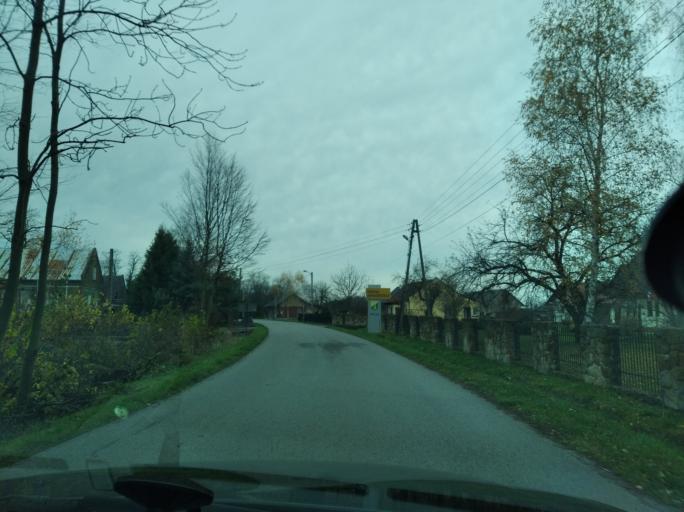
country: PL
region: Subcarpathian Voivodeship
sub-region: Powiat przeworski
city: Nowosielce
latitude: 50.0935
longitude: 22.4164
